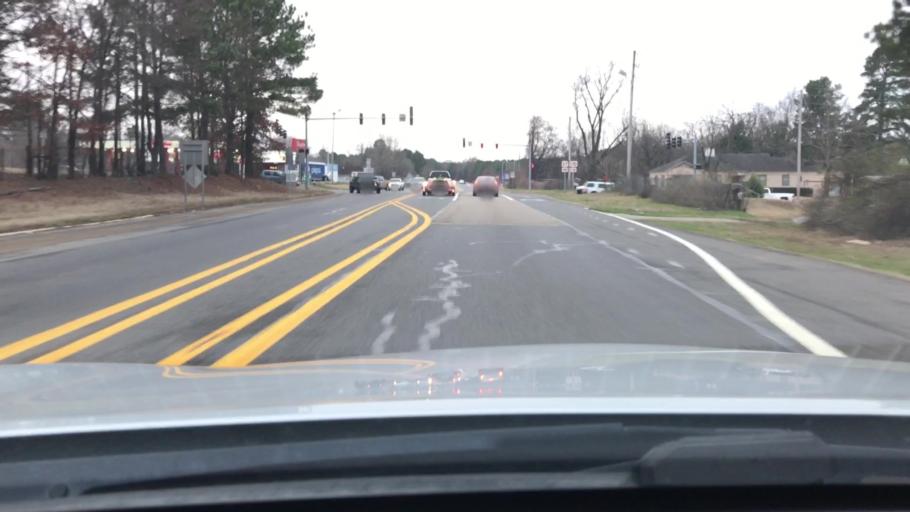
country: US
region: Arkansas
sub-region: Hempstead County
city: Hope
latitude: 33.6690
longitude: -93.5758
